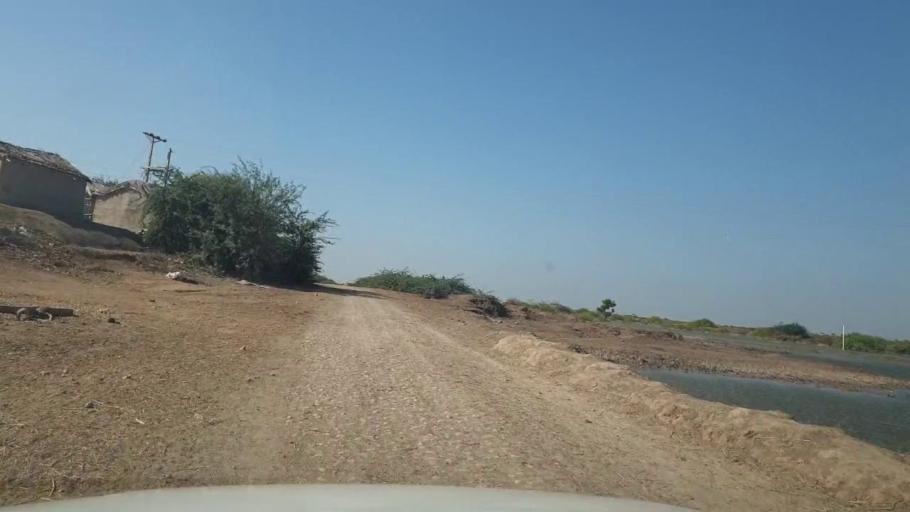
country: PK
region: Sindh
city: Chuhar Jamali
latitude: 24.4396
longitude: 67.8438
